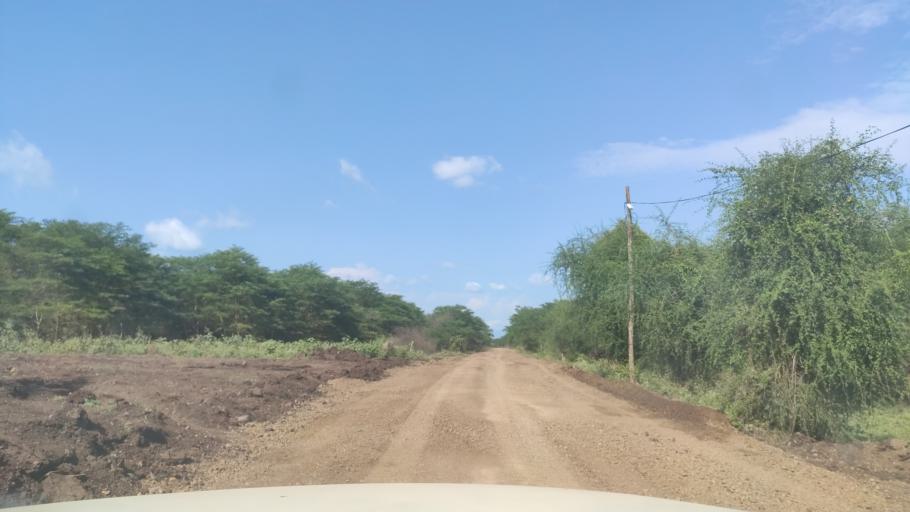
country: ET
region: Southern Nations, Nationalities, and People's Region
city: Felege Neway
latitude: 6.3805
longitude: 37.0914
